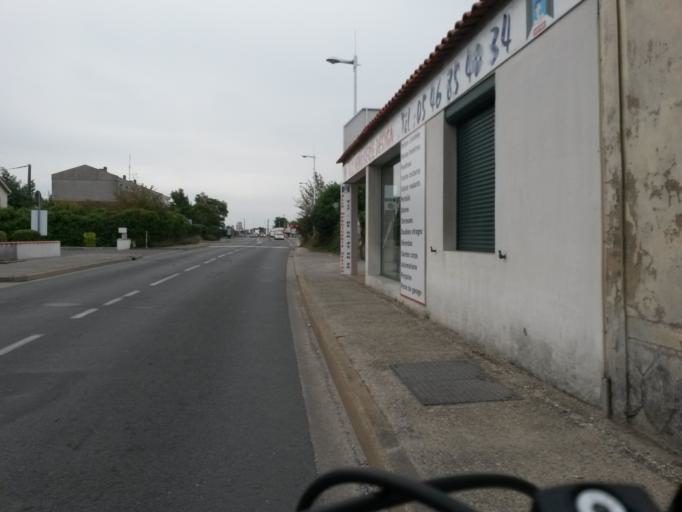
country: FR
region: Poitou-Charentes
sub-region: Departement de la Charente-Maritime
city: Dolus-d'Oleron
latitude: 45.9420
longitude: -1.3148
